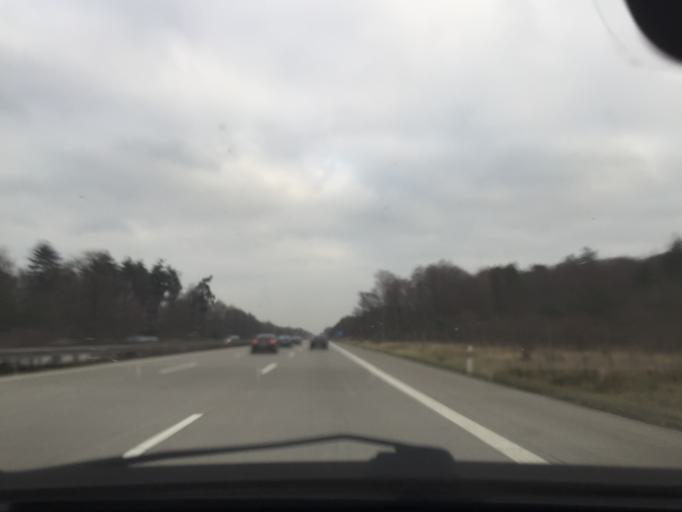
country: DE
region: Saxony-Anhalt
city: Tucheim
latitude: 52.2405
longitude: 12.1190
